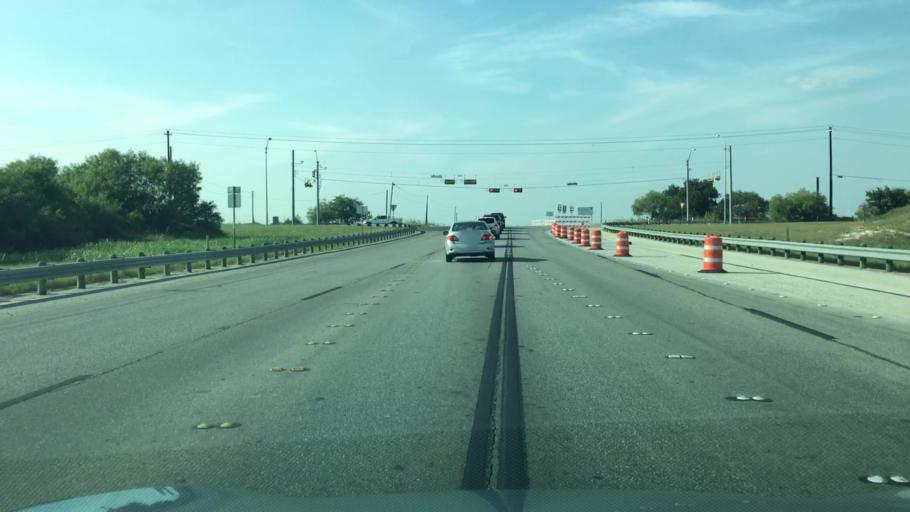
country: US
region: Texas
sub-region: Hays County
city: Buda
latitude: 30.0491
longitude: -97.8748
